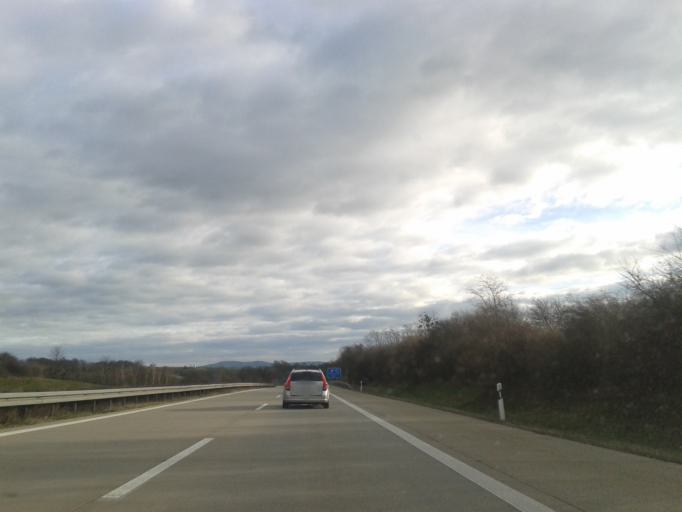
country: DE
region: Saxony
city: Weissenberg
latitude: 51.2079
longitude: 14.6423
